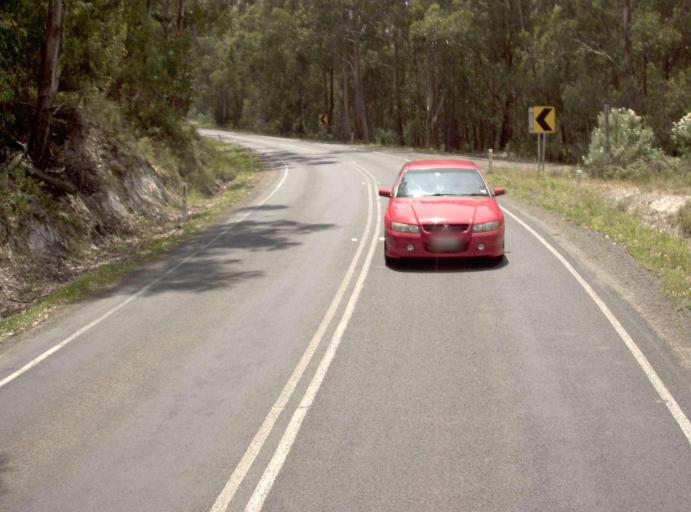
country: AU
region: Victoria
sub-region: Latrobe
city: Traralgon
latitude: -38.3854
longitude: 146.7562
